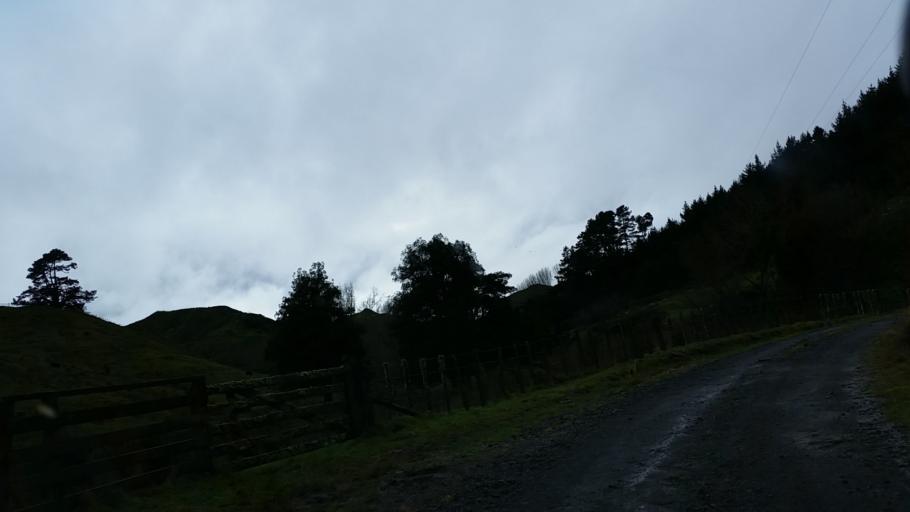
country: NZ
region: Taranaki
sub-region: South Taranaki District
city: Eltham
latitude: -39.4838
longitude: 174.4360
